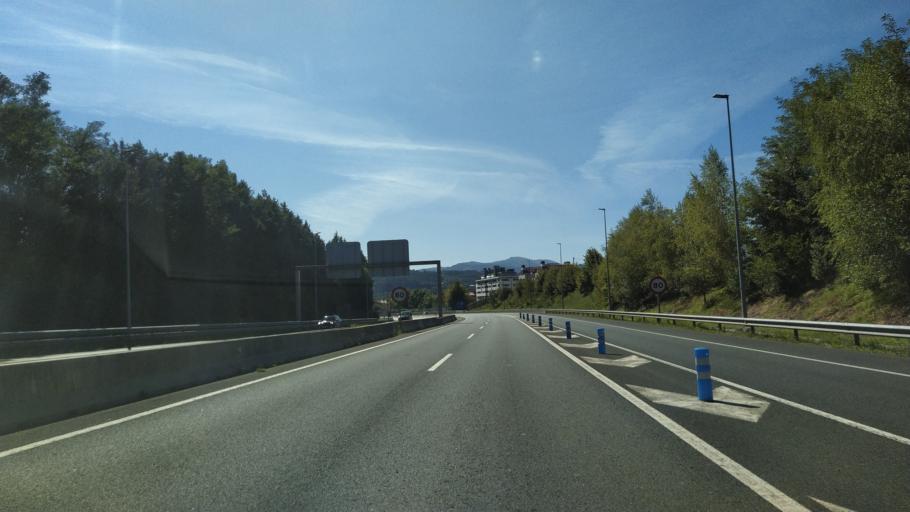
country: ES
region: Basque Country
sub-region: Bizkaia
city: Derio
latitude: 43.3042
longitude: -2.8811
